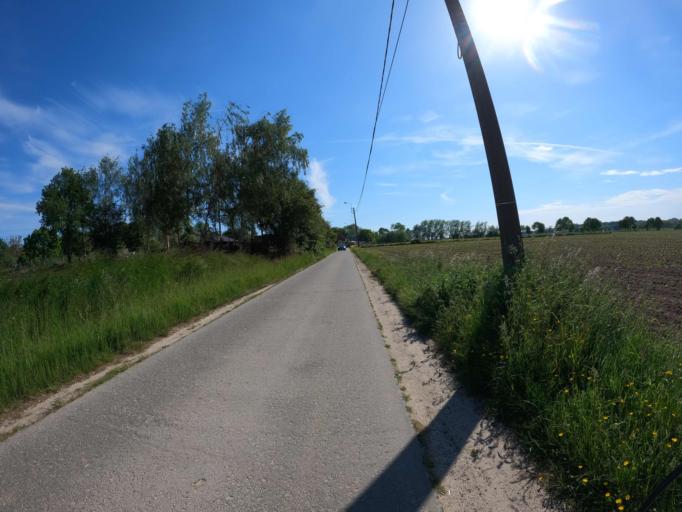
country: BE
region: Flanders
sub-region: Provincie Oost-Vlaanderen
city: Oosterzele
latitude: 50.9201
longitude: 3.7836
